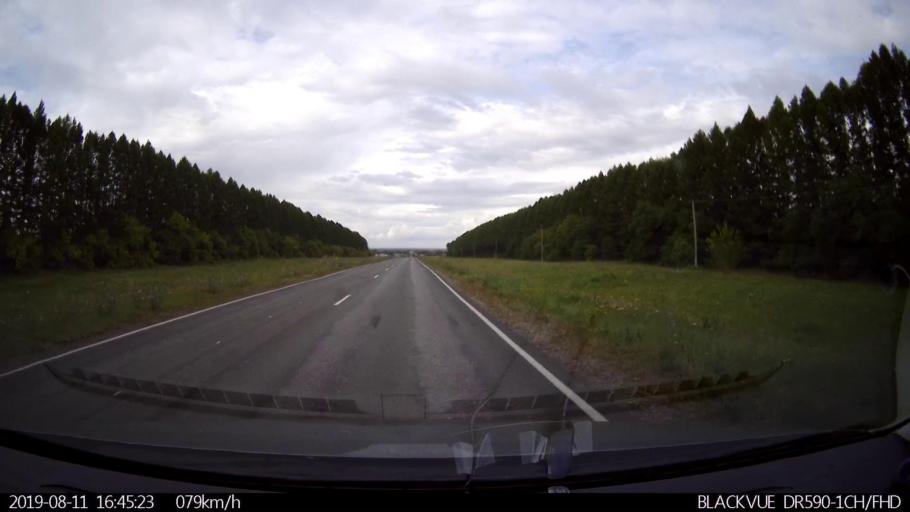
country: RU
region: Ulyanovsk
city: Mayna
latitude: 54.1892
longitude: 47.6857
